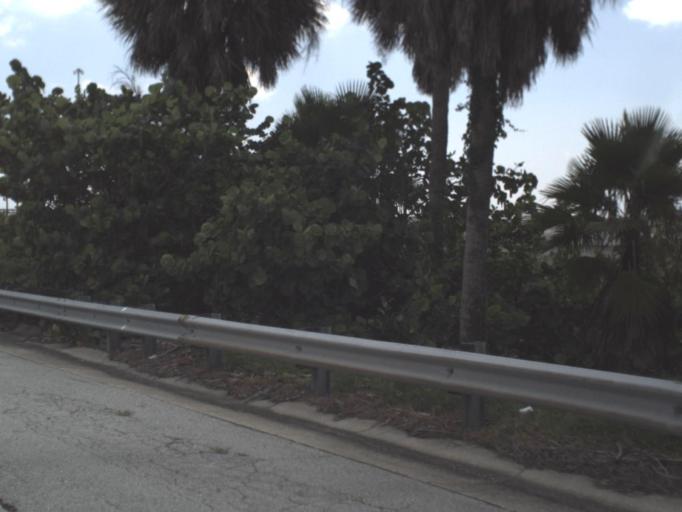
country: US
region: Florida
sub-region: Pinellas County
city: Feather Sound
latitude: 27.8783
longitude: -82.6592
